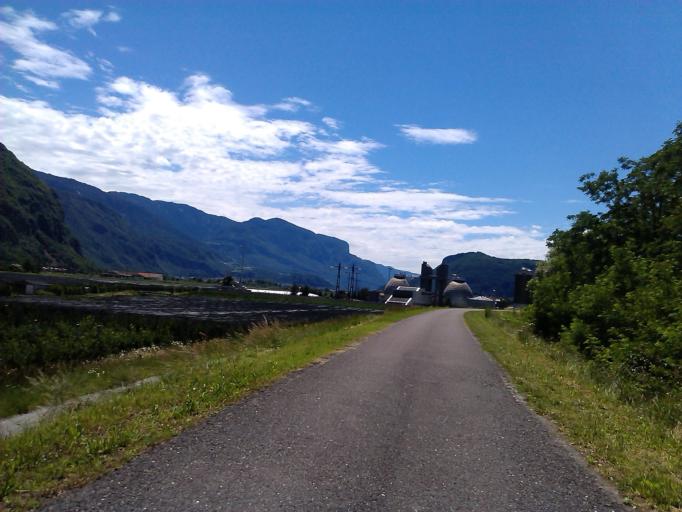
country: IT
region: Trentino-Alto Adige
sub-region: Bolzano
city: Vadena
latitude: 46.4106
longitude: 11.3140
